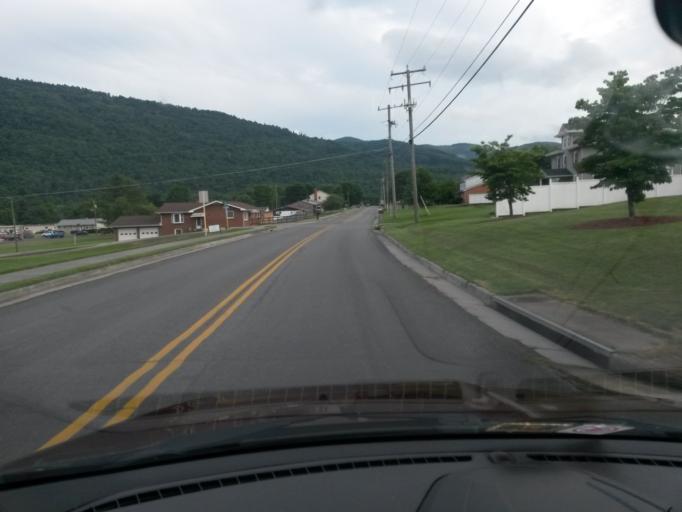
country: US
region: Virginia
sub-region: City of Covington
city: Fairlawn
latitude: 37.7674
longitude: -79.9702
